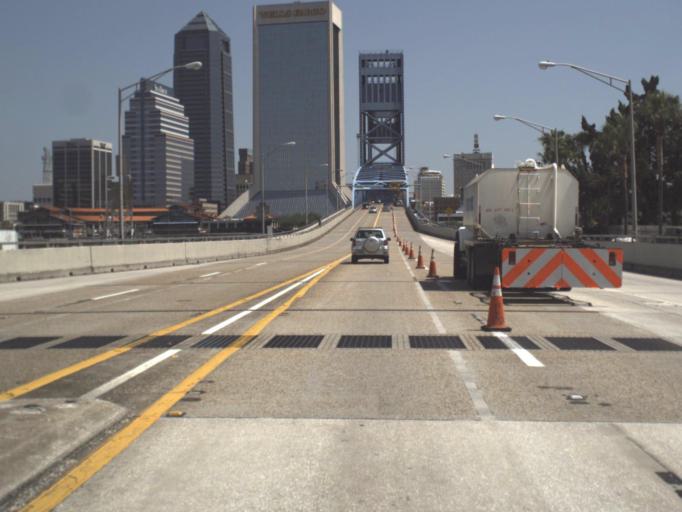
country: US
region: Florida
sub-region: Duval County
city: Jacksonville
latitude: 30.3196
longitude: -81.6588
